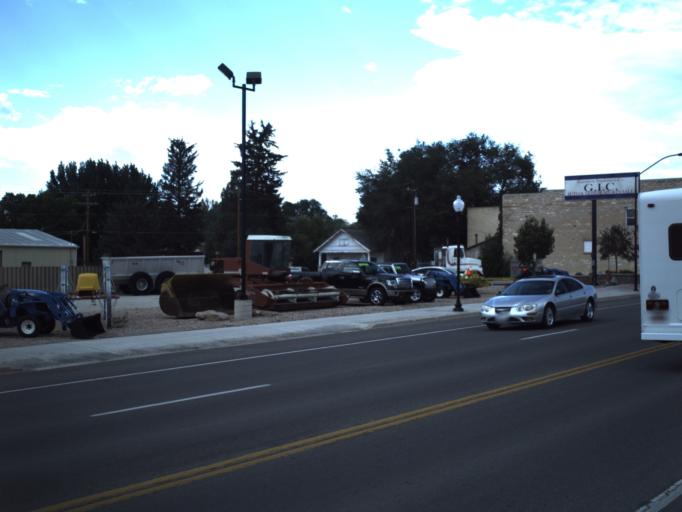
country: US
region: Utah
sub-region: Sanpete County
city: Gunnison
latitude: 39.1530
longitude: -111.8183
